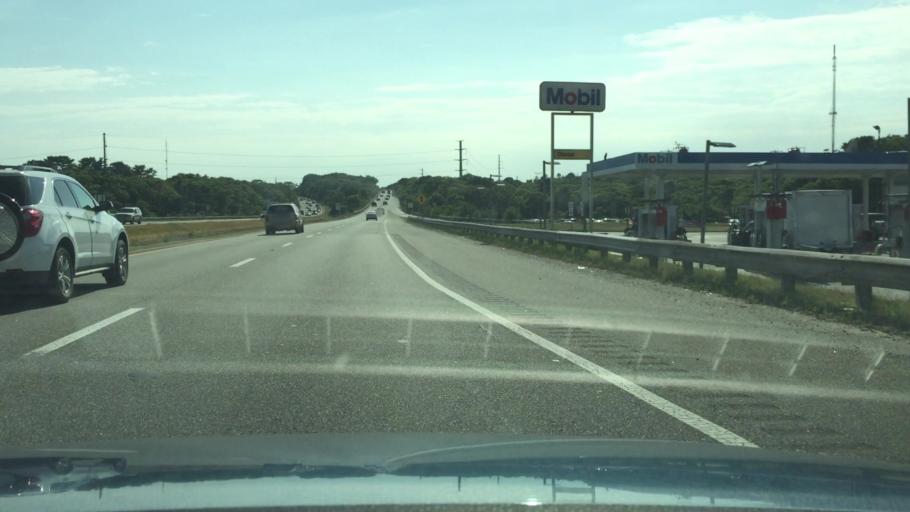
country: US
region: Massachusetts
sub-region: Barnstable County
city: Barnstable
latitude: 41.6874
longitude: -70.3371
